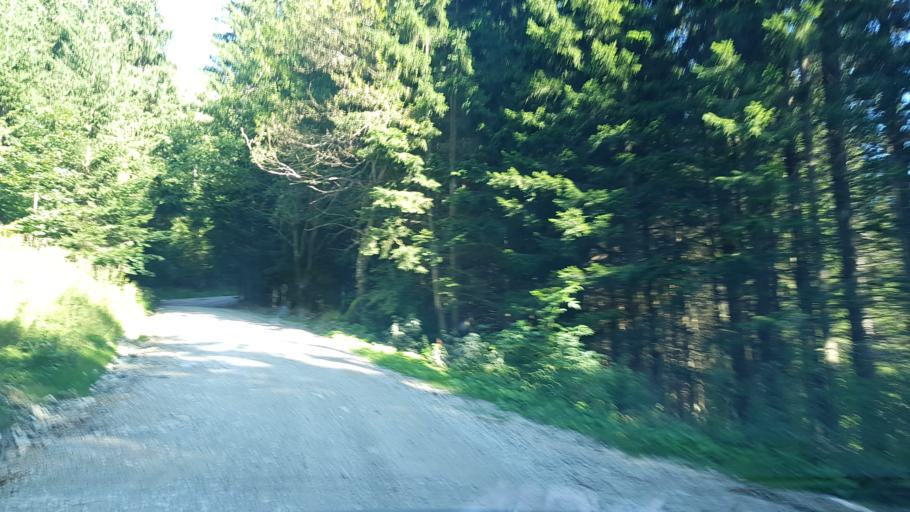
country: SI
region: Ravne na Koroskem
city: Kotlje
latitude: 46.4776
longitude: 14.9595
